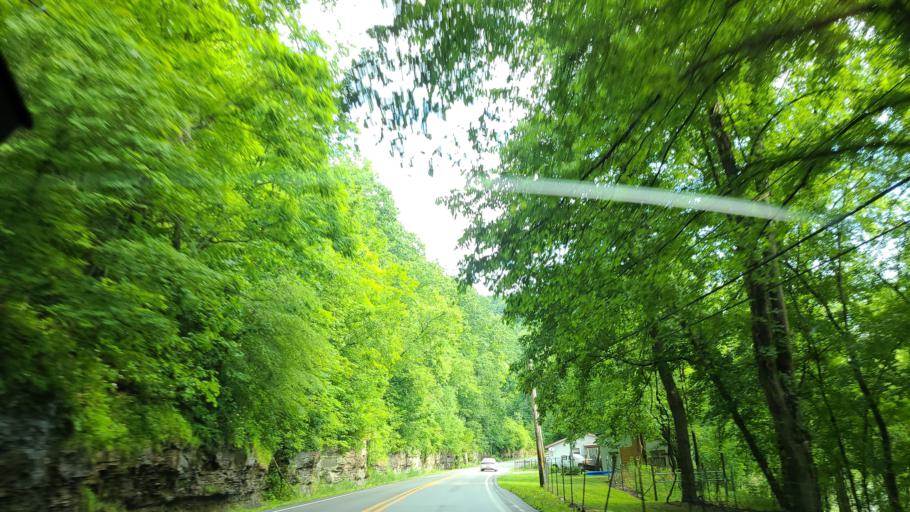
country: US
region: Kentucky
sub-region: Whitley County
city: Williamsburg
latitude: 36.7354
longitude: -84.1062
